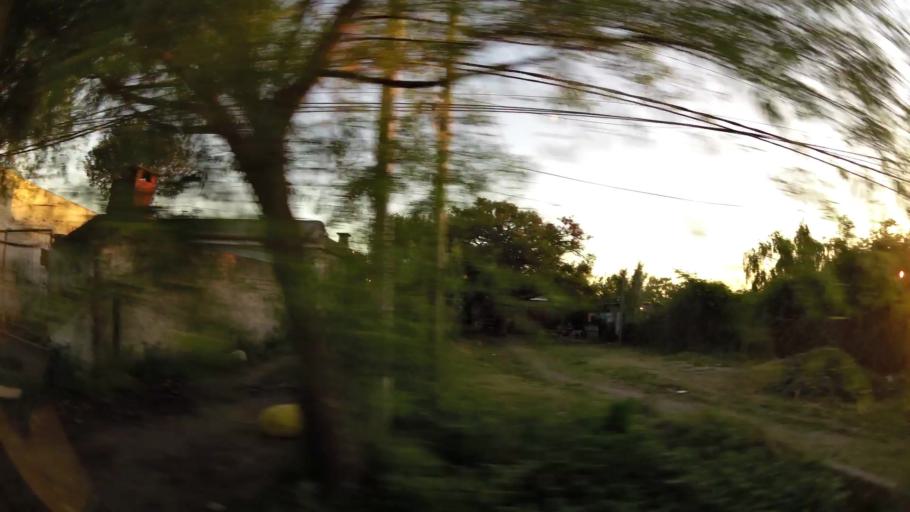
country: UY
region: Montevideo
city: Montevideo
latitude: -34.8291
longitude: -56.1568
